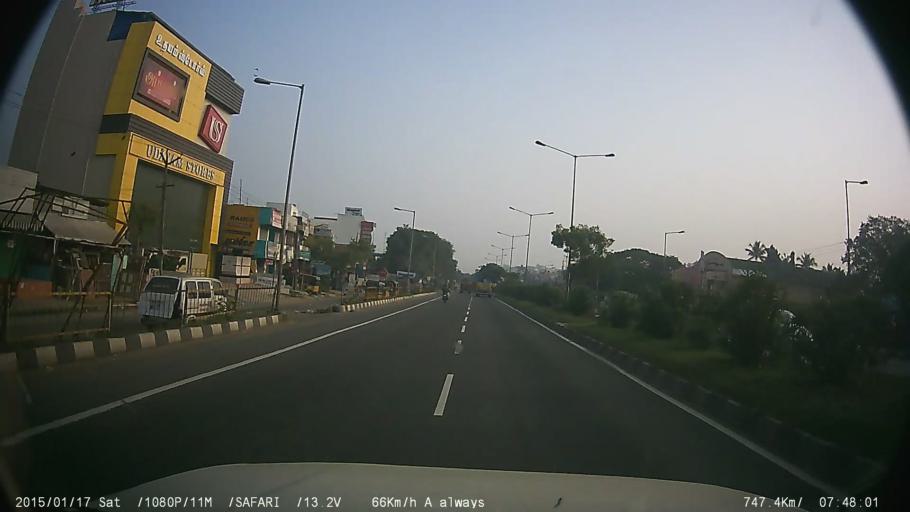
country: IN
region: Tamil Nadu
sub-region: Kancheepuram
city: Guduvancheri
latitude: 12.8475
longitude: 80.0629
